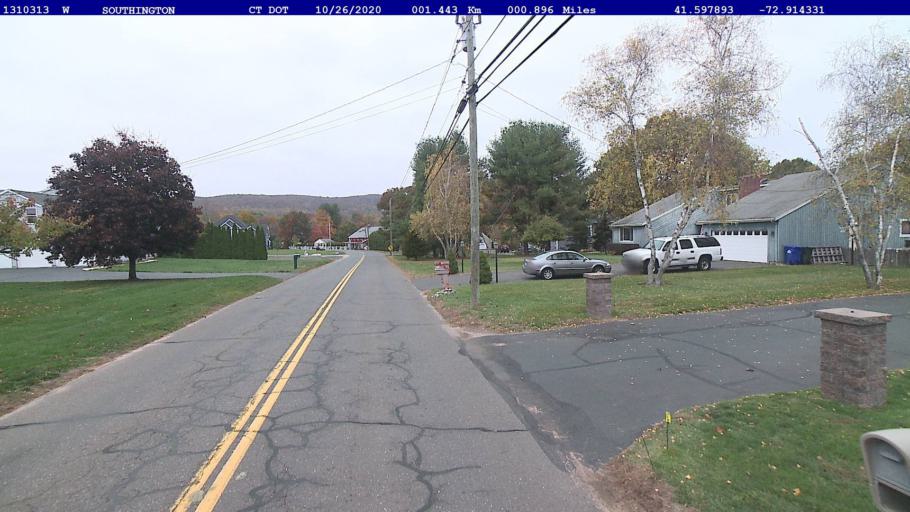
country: US
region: Connecticut
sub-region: New Haven County
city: Wolcott
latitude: 41.5979
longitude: -72.9143
